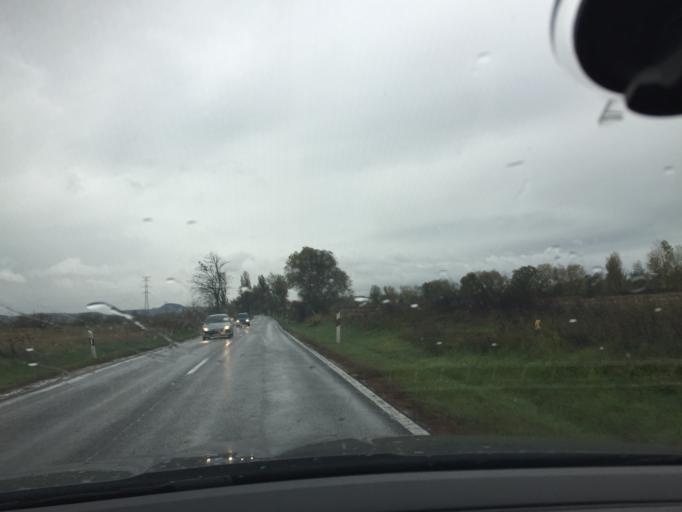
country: SK
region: Nitriansky
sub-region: Okres Nove Zamky
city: Sturovo
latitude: 47.7675
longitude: 18.7090
